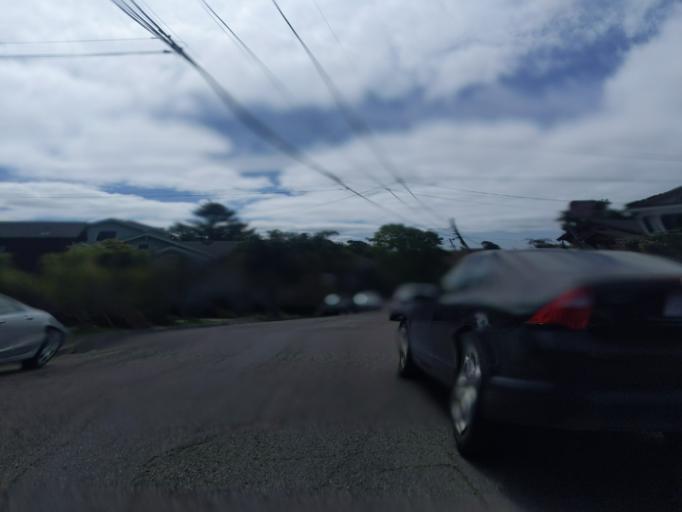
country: US
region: California
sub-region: Alameda County
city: Alameda
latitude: 37.7886
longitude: -122.2276
